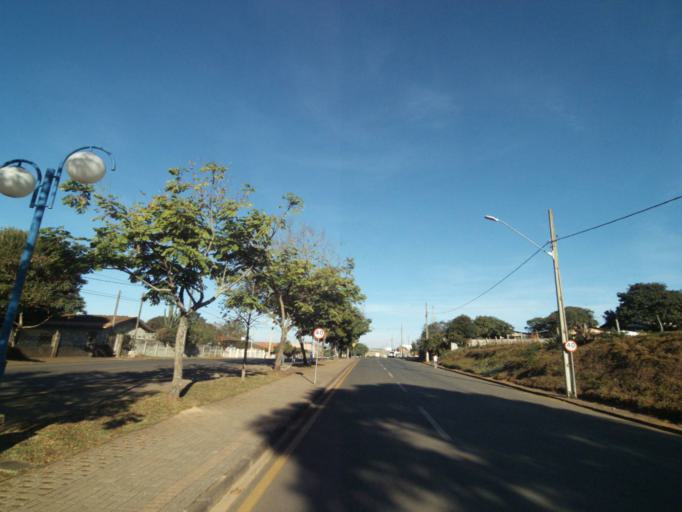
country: BR
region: Parana
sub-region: Tibagi
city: Tibagi
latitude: -24.5222
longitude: -50.4102
